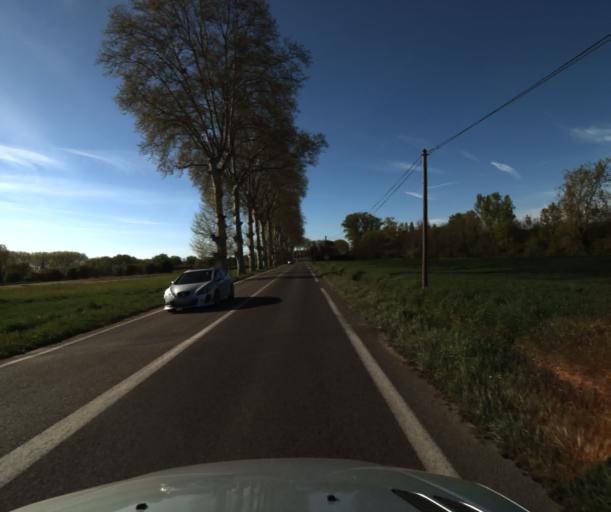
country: FR
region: Midi-Pyrenees
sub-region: Departement du Tarn-et-Garonne
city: Lafrancaise
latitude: 44.0819
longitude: 1.2778
